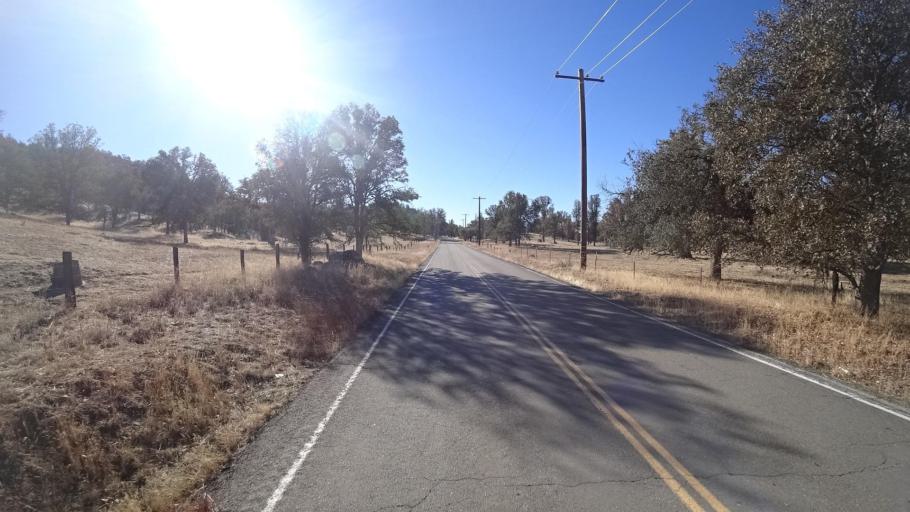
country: US
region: California
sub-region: Kern County
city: Alta Sierra
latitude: 35.7550
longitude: -118.7149
